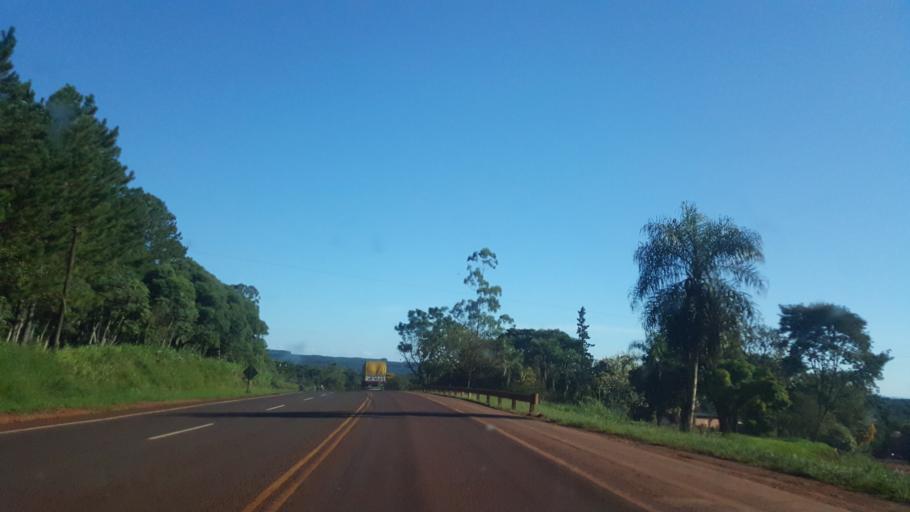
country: AR
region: Misiones
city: Puerto Esperanza
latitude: -26.1800
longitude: -54.5894
